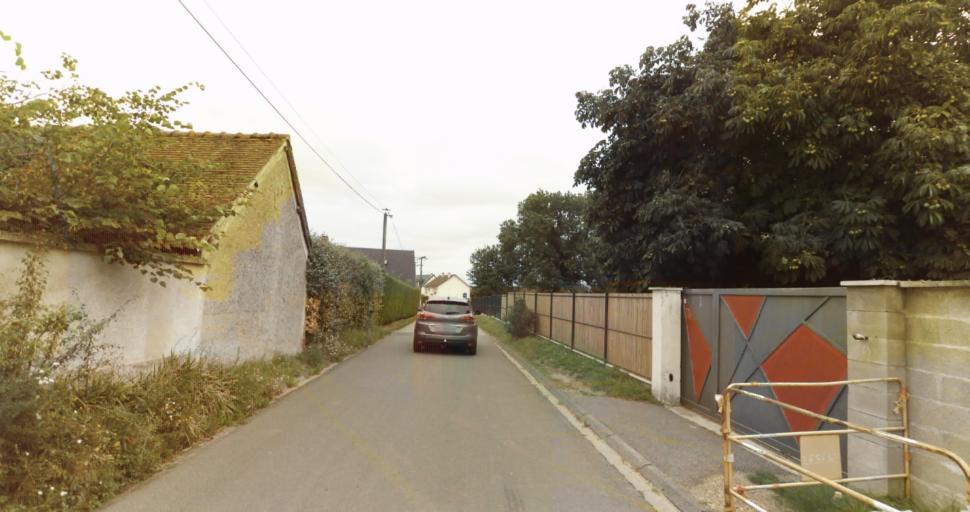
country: FR
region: Haute-Normandie
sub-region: Departement de l'Eure
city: Evreux
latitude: 48.9614
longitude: 1.2521
